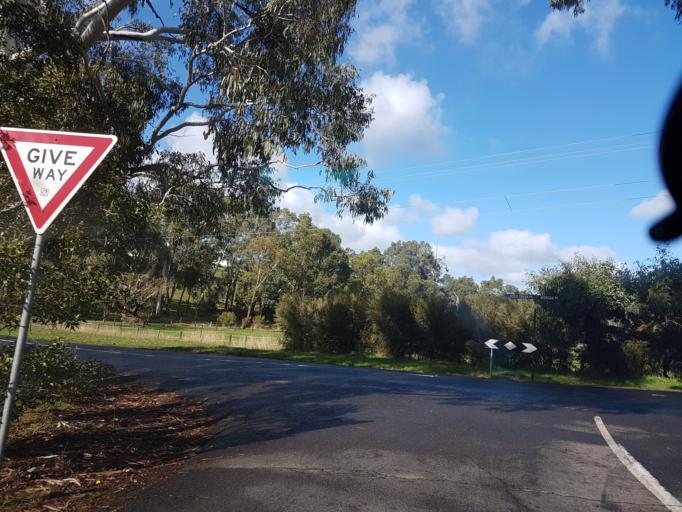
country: AU
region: South Australia
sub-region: Adelaide Hills
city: Heathfield
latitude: -35.0426
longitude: 138.7096
